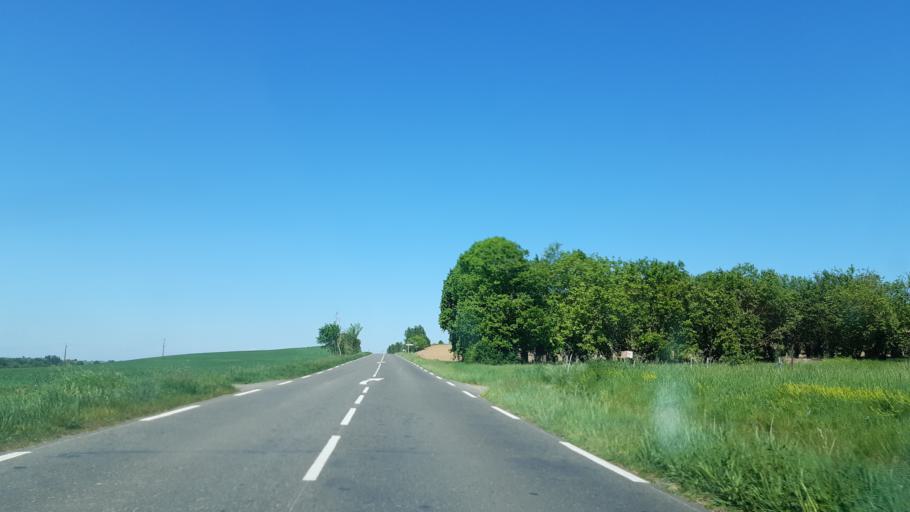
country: FR
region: Midi-Pyrenees
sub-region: Departement du Gers
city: Pujaudran
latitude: 43.5782
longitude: 1.0420
